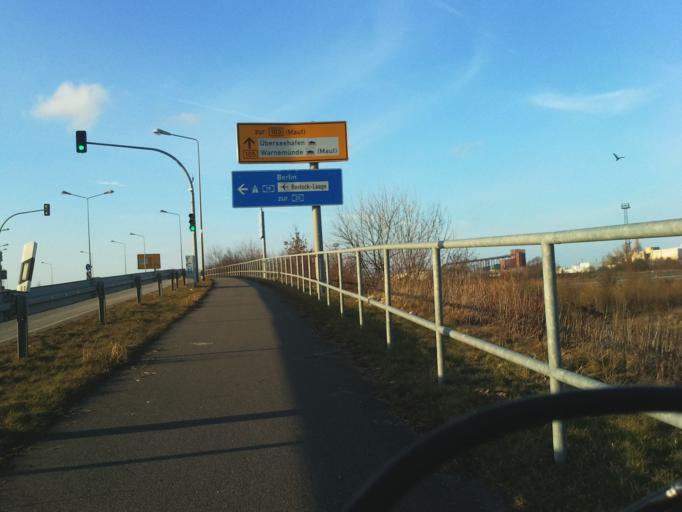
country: DE
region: Mecklenburg-Vorpommern
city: Dierkow-West
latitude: 54.1367
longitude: 12.1204
